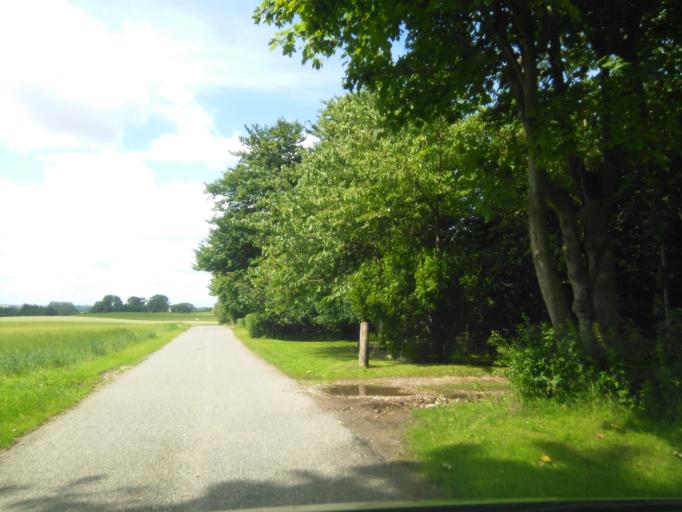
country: DK
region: Central Jutland
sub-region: Syddjurs Kommune
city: Ronde
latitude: 56.2366
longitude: 10.4703
